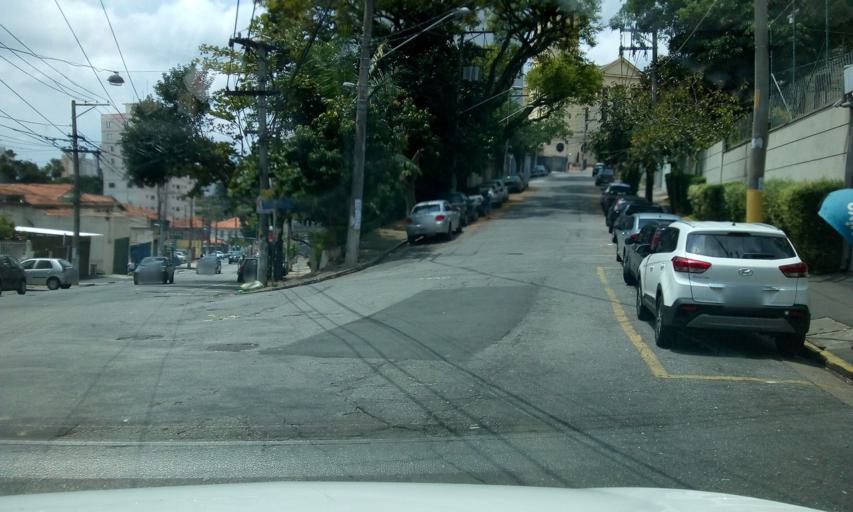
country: BR
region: Sao Paulo
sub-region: Sao Paulo
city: Sao Paulo
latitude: -23.5746
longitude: -46.6330
